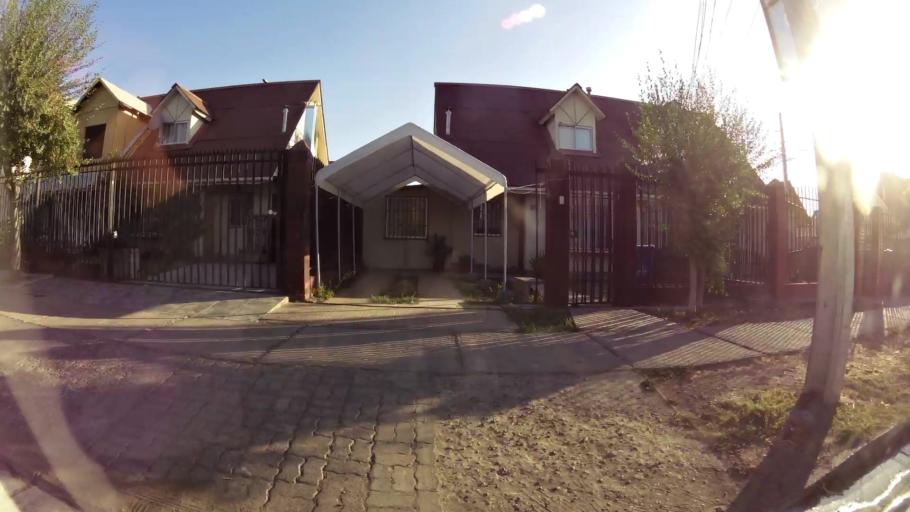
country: CL
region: Maule
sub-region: Provincia de Talca
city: Talca
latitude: -35.4501
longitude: -71.6757
